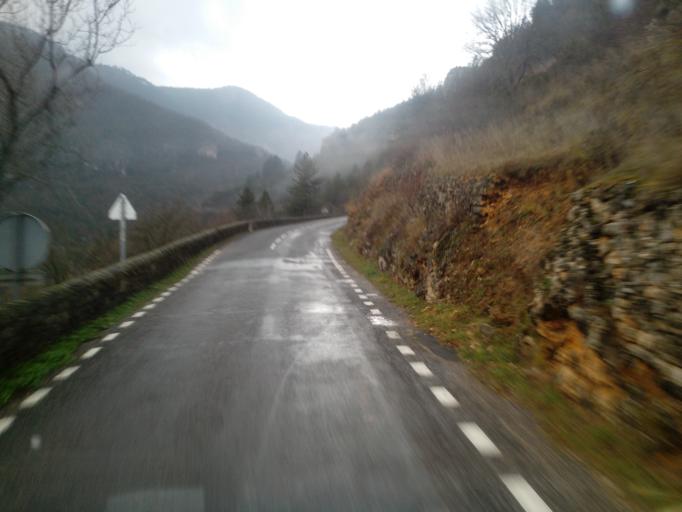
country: FR
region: Languedoc-Roussillon
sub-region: Departement de la Lozere
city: Florac
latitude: 44.3538
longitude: 3.4554
